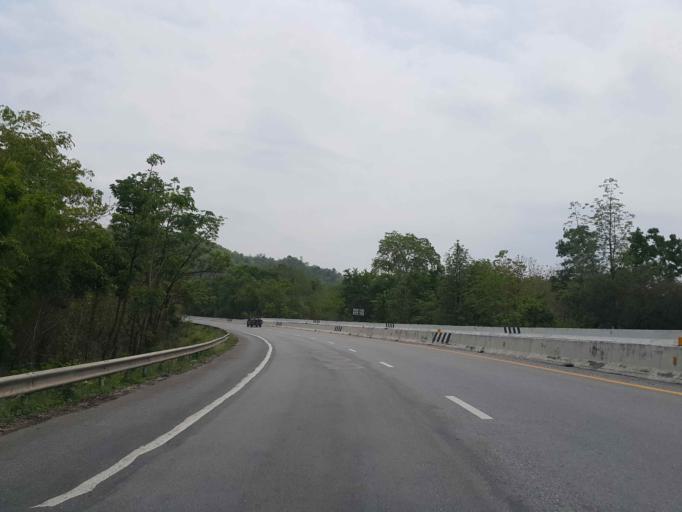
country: TH
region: Lampang
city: Sop Prap
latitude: 17.8361
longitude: 99.2907
